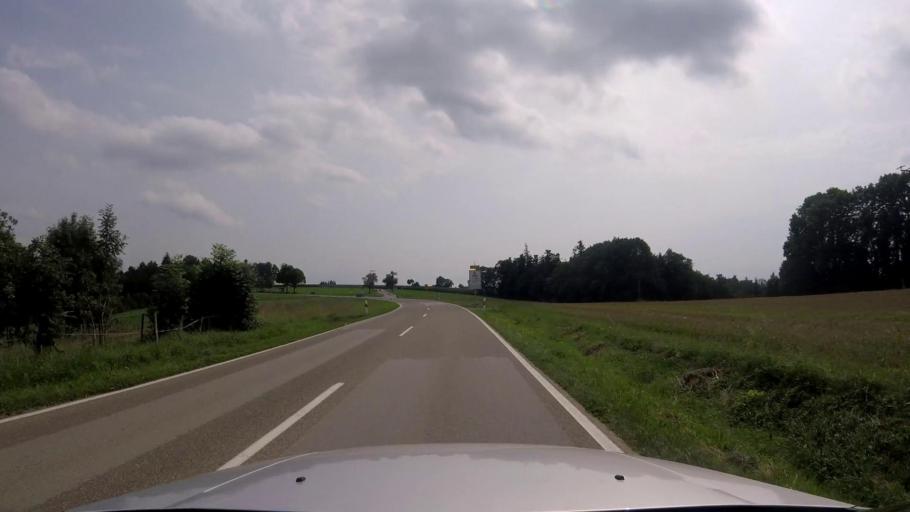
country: DE
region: Baden-Wuerttemberg
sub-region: Regierungsbezirk Stuttgart
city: Gschwend
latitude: 48.9169
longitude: 9.7275
